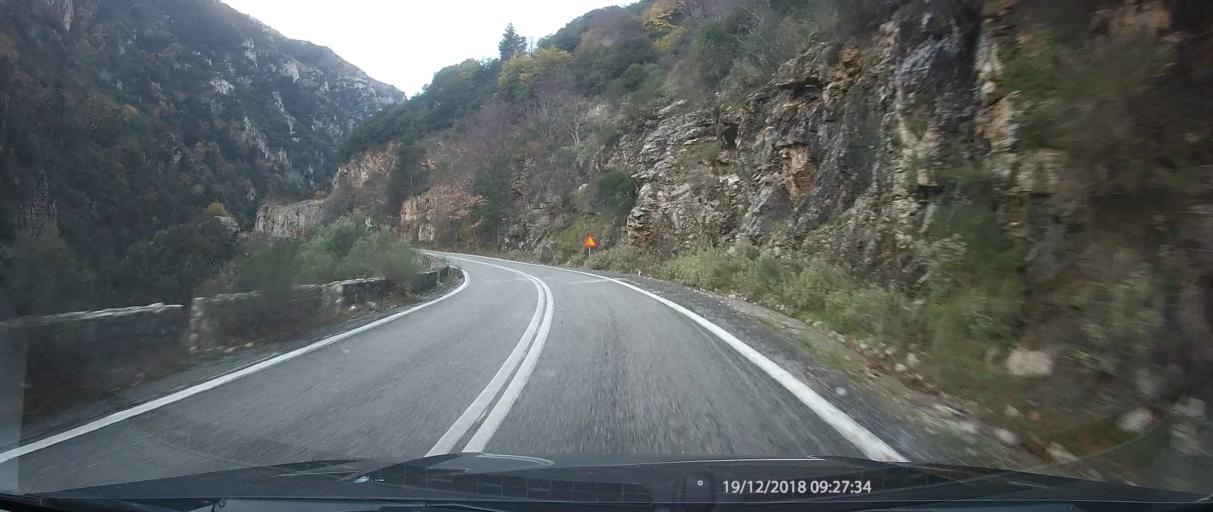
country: GR
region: Peloponnese
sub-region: Nomos Lakonias
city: Magoula
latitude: 37.0913
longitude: 22.3243
